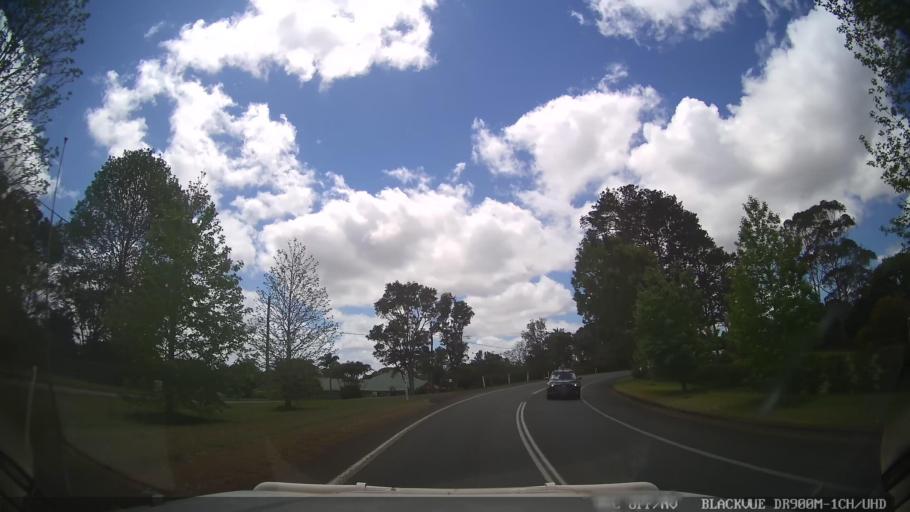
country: AU
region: Queensland
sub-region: Sunshine Coast
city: Nambour
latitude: -26.6639
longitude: 152.8798
